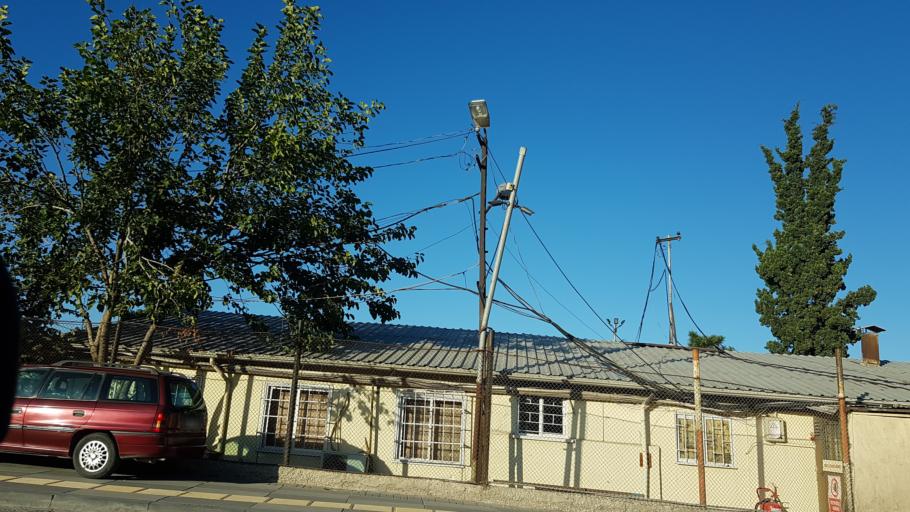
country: TR
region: Ankara
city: Ankara
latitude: 39.9531
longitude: 32.8328
